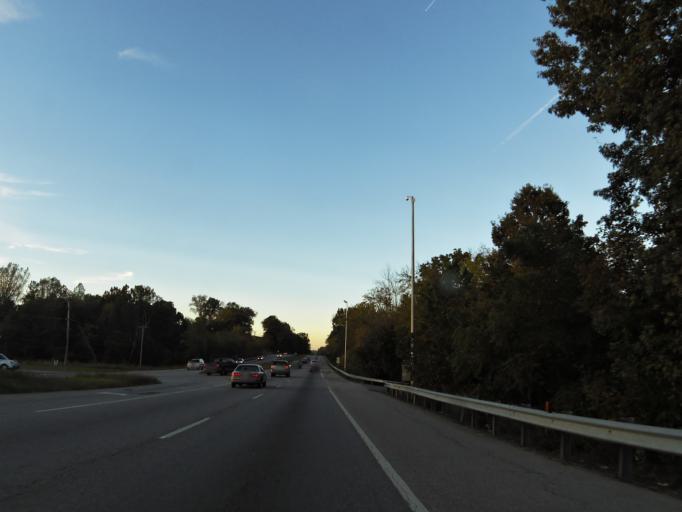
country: US
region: Tennessee
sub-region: Blount County
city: Eagleton Village
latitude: 35.8660
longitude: -83.9595
